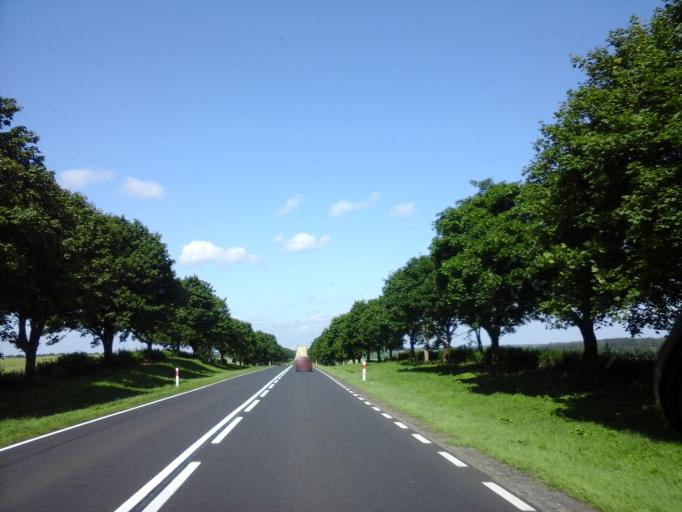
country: PL
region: West Pomeranian Voivodeship
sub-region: Powiat stargardzki
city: Dobrzany
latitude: 53.2726
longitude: 15.4289
